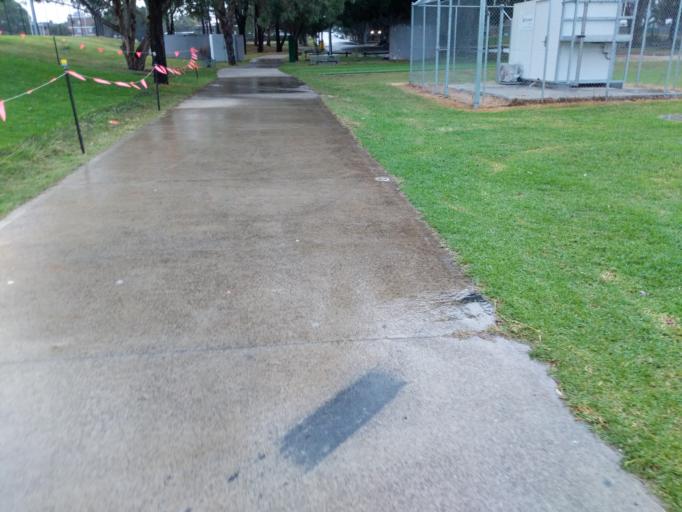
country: AU
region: New South Wales
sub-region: Ashfield
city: Croydon
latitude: -33.8656
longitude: 151.1103
